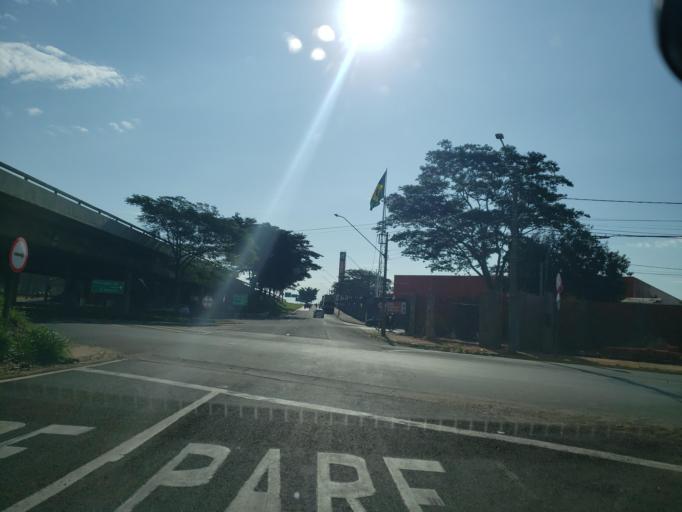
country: BR
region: Sao Paulo
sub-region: Aracatuba
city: Aracatuba
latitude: -21.2124
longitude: -50.4668
